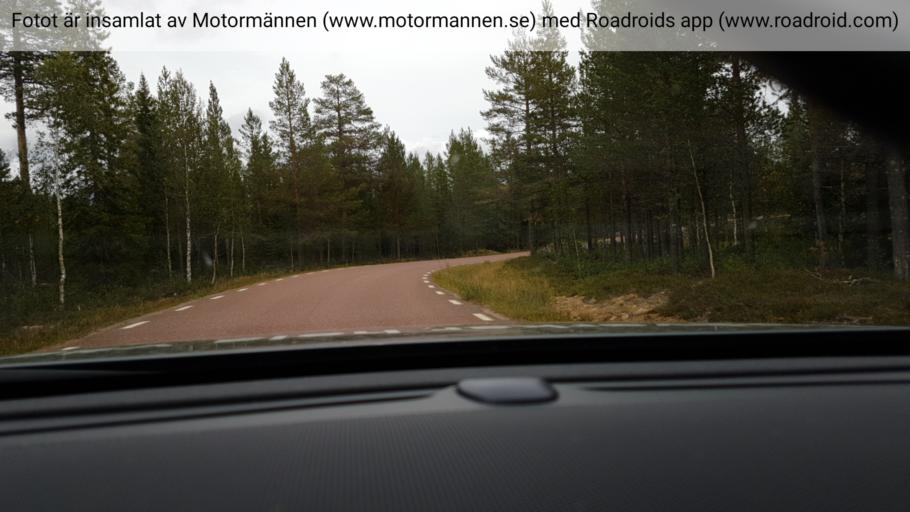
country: NO
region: Hedmark
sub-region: Trysil
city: Innbygda
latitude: 61.6971
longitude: 12.6304
